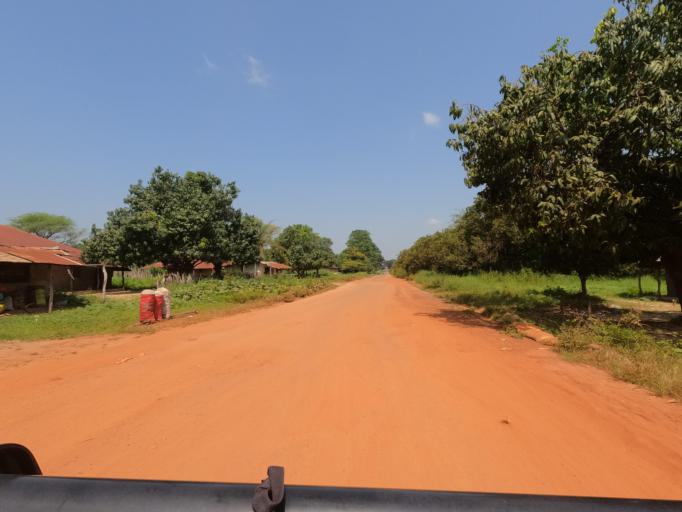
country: GW
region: Oio
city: Bissora
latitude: 12.3659
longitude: -15.7749
